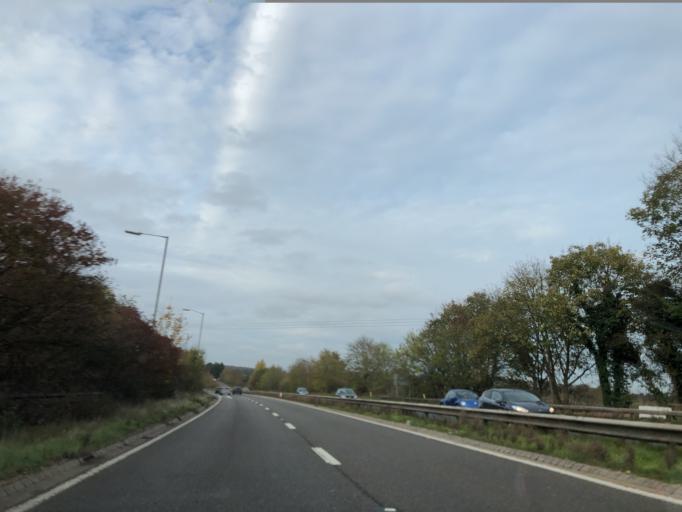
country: GB
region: England
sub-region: Buckinghamshire
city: Marlow
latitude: 51.5757
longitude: -0.7564
